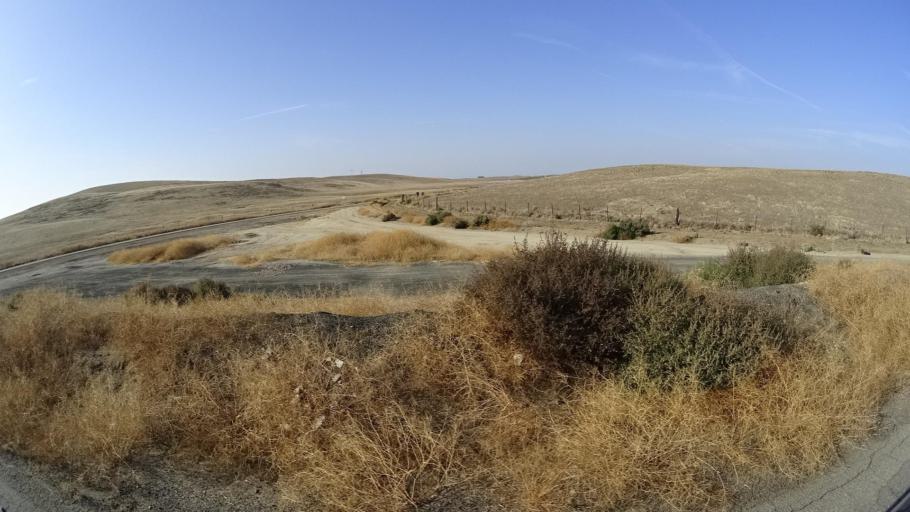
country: US
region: California
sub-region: Tulare County
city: Richgrove
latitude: 35.6220
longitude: -119.0294
